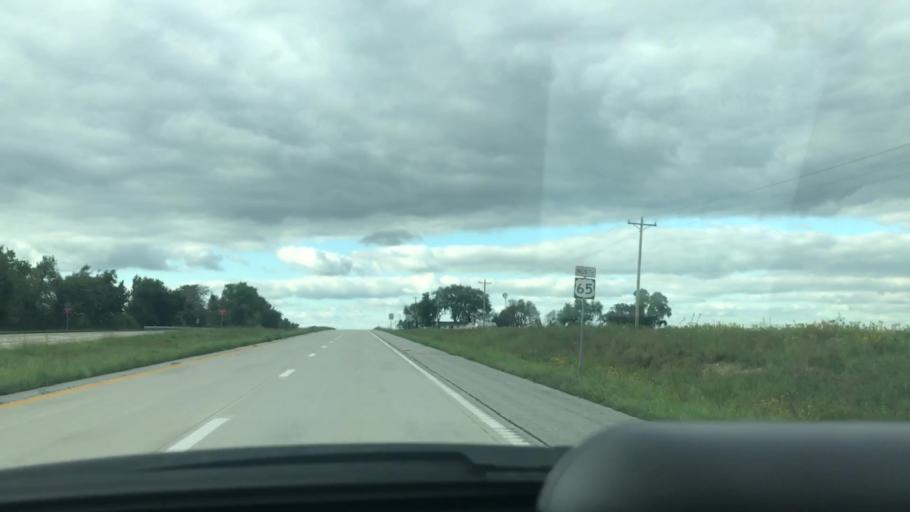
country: US
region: Missouri
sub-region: Benton County
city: Lincoln
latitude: 38.3662
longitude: -93.3389
